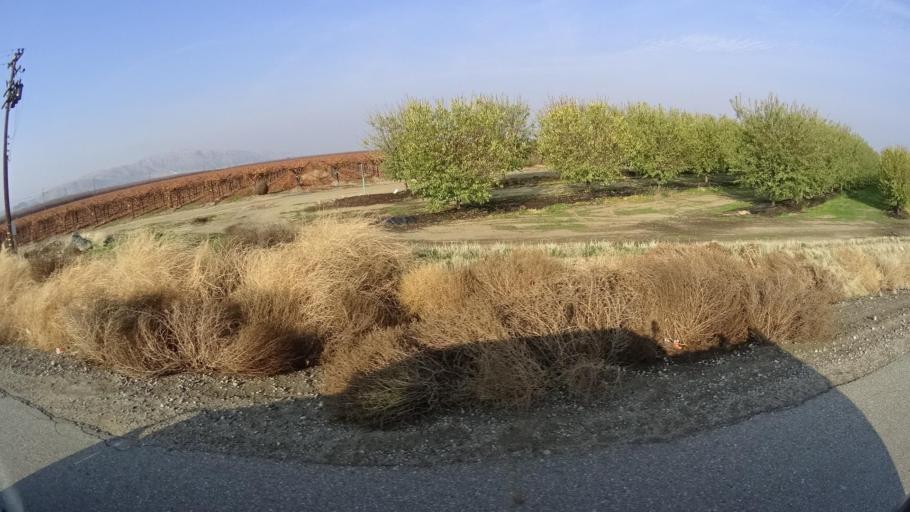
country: US
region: California
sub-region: Kern County
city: Lebec
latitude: 35.0177
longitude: -118.9351
